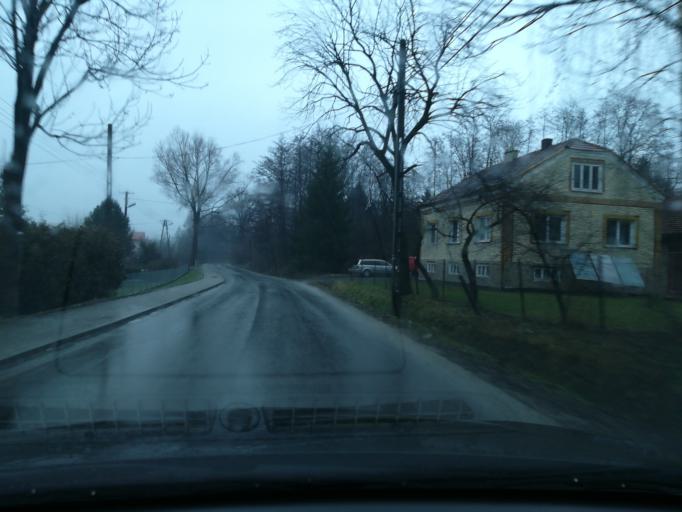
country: PL
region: Subcarpathian Voivodeship
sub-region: Powiat lancucki
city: Kosina
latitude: 50.0760
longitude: 22.3291
